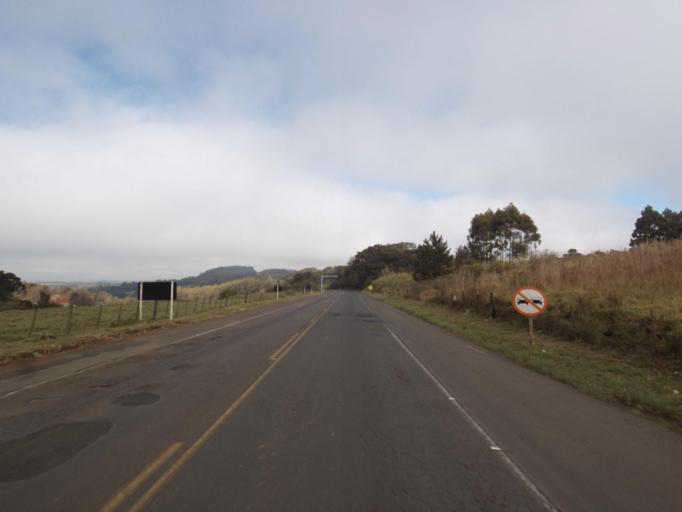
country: BR
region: Rio Grande do Sul
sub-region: Frederico Westphalen
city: Frederico Westphalen
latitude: -27.1049
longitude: -53.2133
